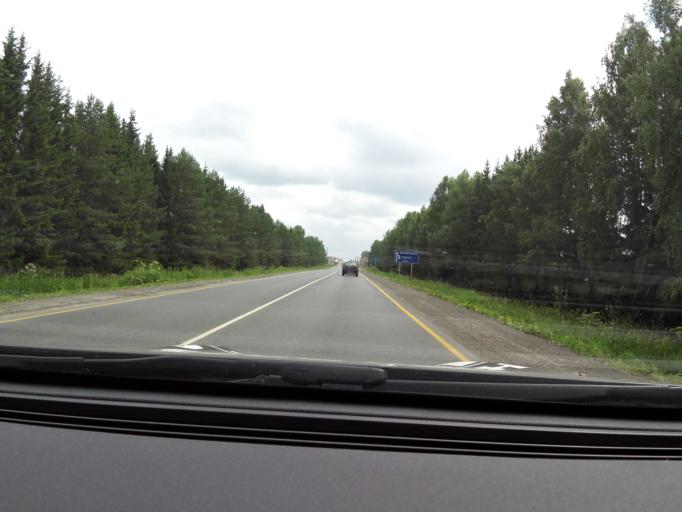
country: RU
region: Perm
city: Kungur
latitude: 57.4110
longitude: 56.8714
